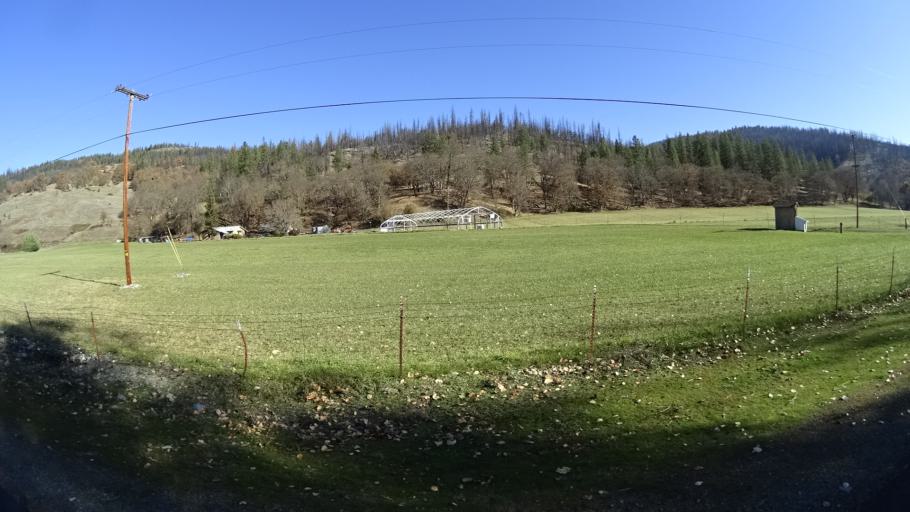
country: US
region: California
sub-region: Siskiyou County
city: Happy Camp
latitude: 41.8382
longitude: -123.0136
